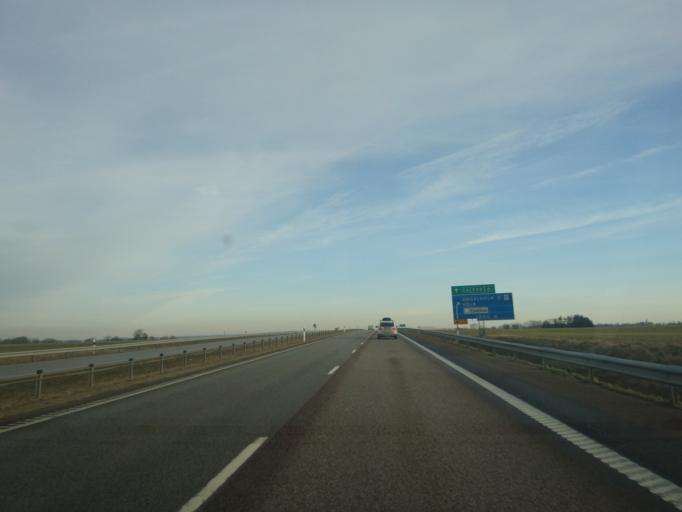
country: SE
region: Skane
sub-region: Angelholms Kommun
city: AEngelholm
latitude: 56.2142
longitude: 12.8881
